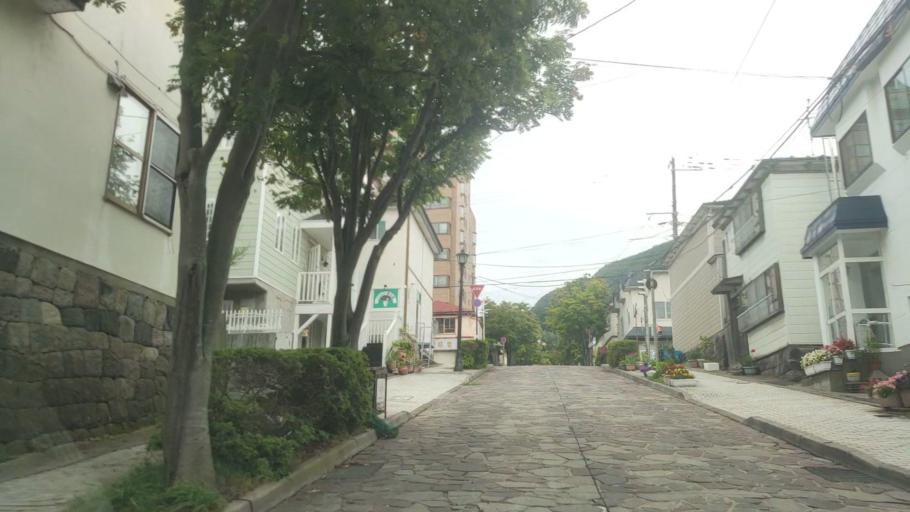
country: JP
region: Hokkaido
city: Hakodate
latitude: 41.7645
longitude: 140.7149
